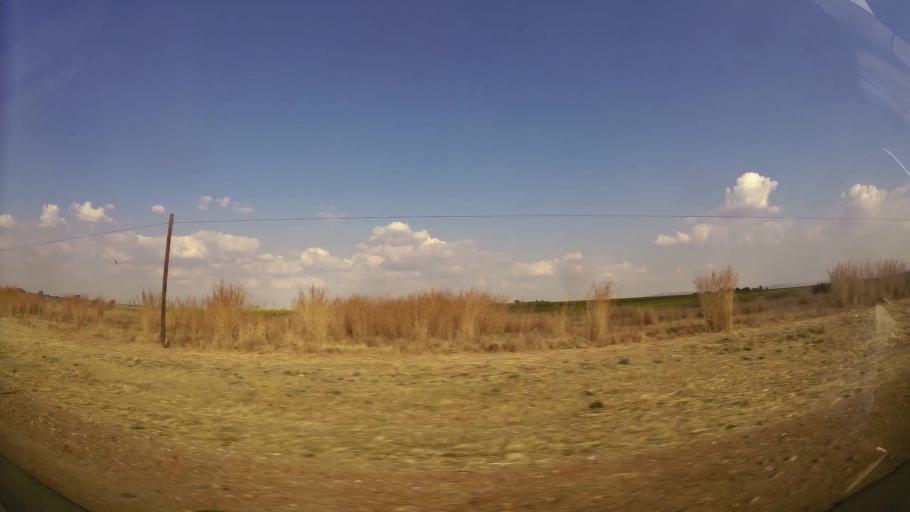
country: ZA
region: Gauteng
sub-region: Sedibeng District Municipality
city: Heidelberg
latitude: -26.3865
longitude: 28.3026
